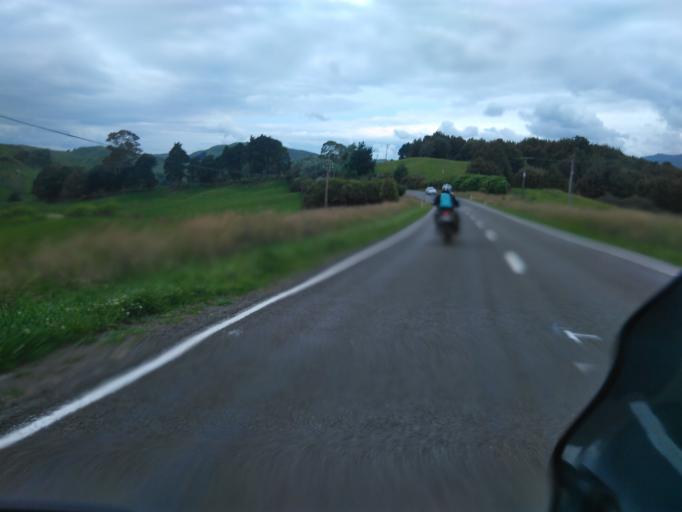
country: NZ
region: Bay of Plenty
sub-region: Opotiki District
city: Opotiki
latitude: -38.3906
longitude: 177.5571
